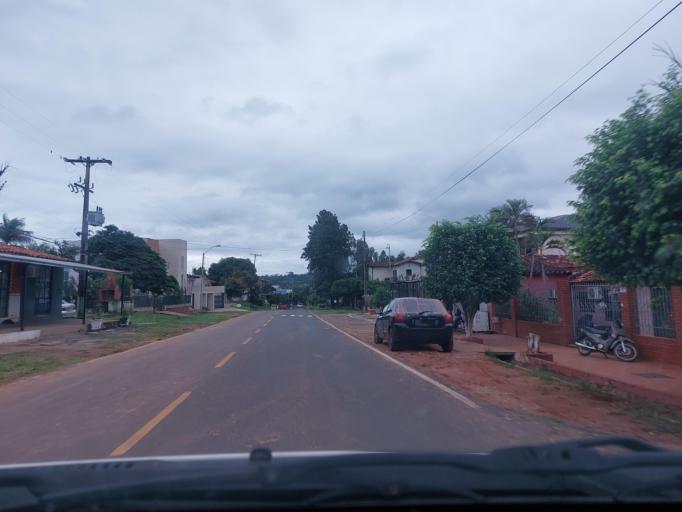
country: PY
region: San Pedro
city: Guayaybi
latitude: -24.6589
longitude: -56.4392
